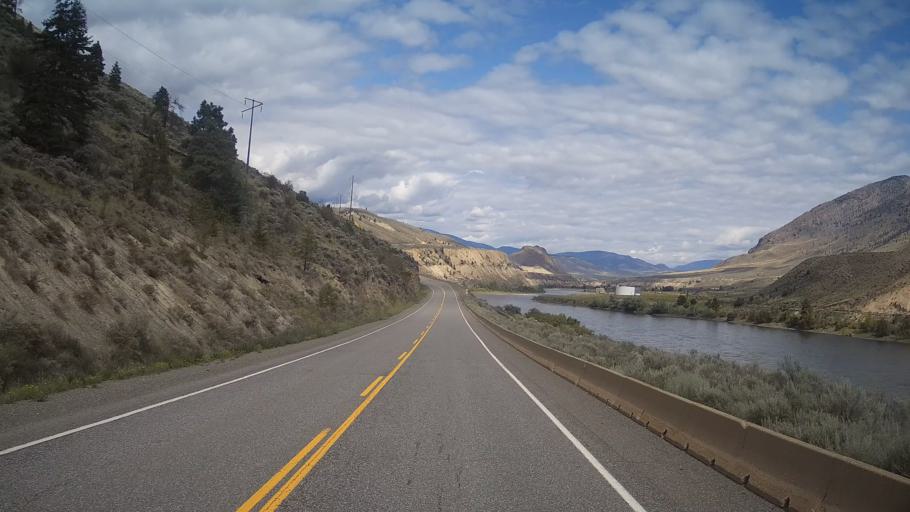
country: CA
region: British Columbia
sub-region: Thompson-Nicola Regional District
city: Ashcroft
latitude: 50.5469
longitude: -121.2927
